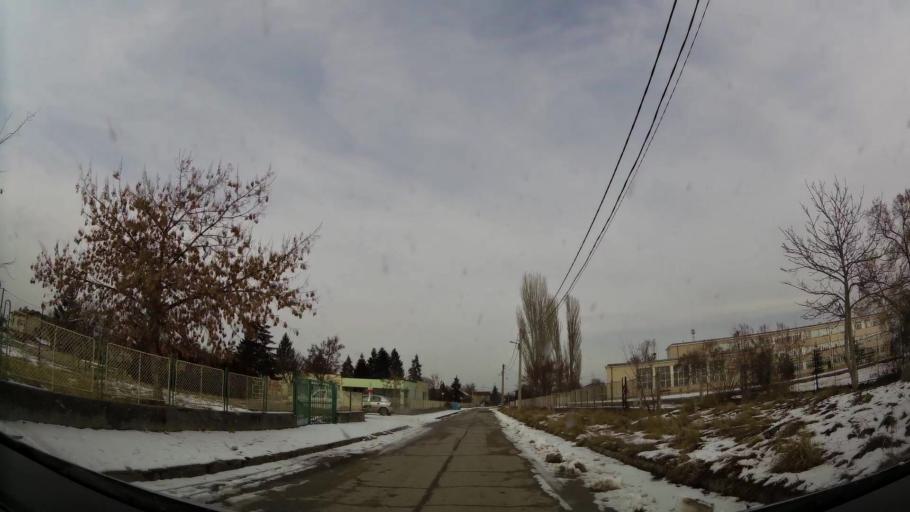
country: BG
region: Sofia-Capital
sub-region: Stolichna Obshtina
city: Sofia
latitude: 42.7105
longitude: 23.4141
